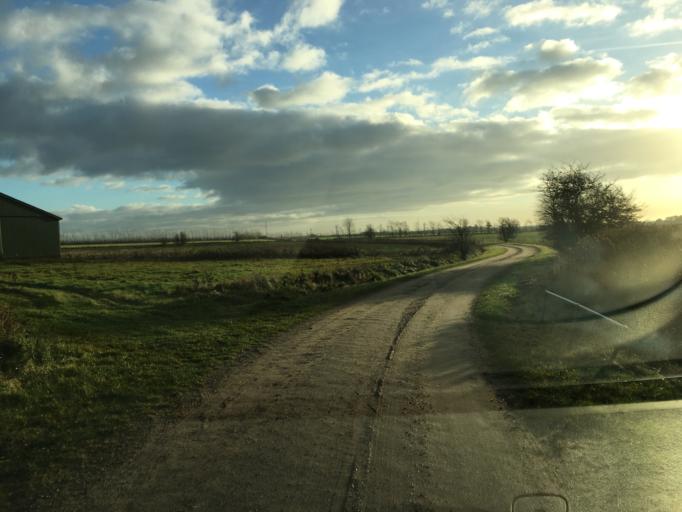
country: DK
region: South Denmark
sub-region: Tonder Kommune
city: Sherrebek
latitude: 55.1537
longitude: 8.8226
